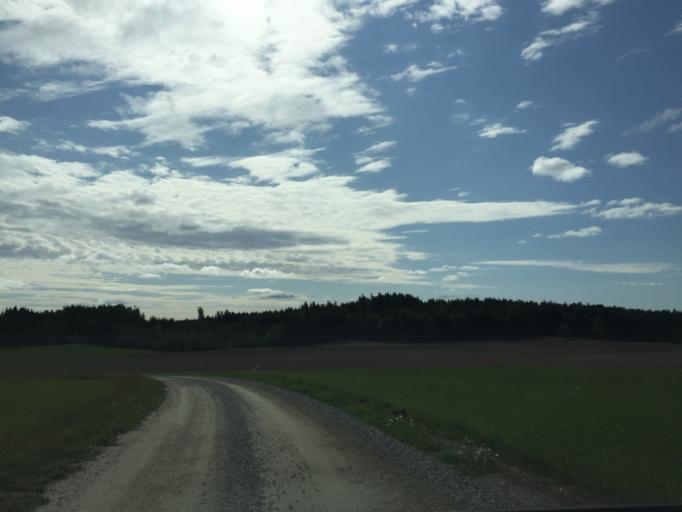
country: NO
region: Ostfold
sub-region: Hobol
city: Elvestad
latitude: 59.6325
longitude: 10.8888
